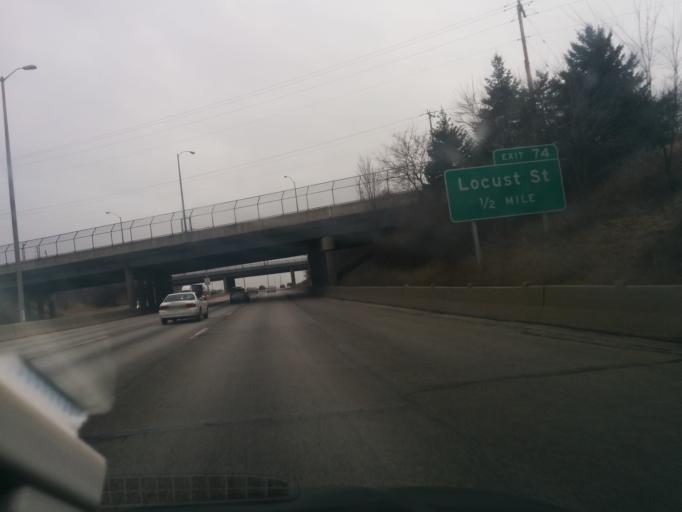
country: US
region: Wisconsin
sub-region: Milwaukee County
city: Shorewood
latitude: 43.0833
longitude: -87.9206
